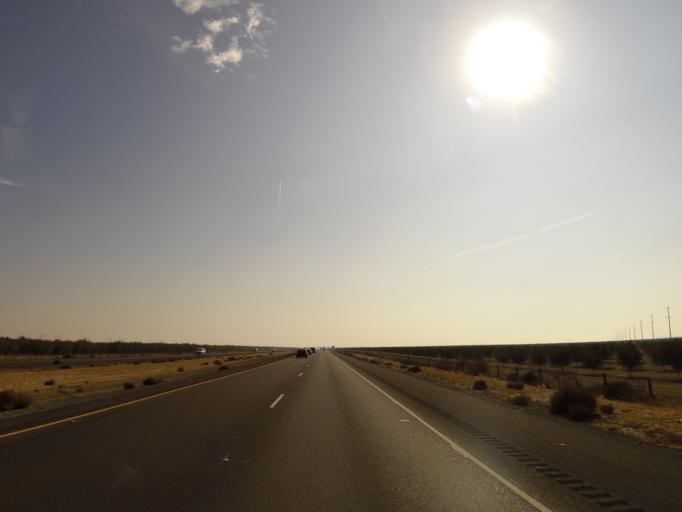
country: US
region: California
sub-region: Kings County
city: Kettleman City
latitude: 35.9460
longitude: -119.9240
